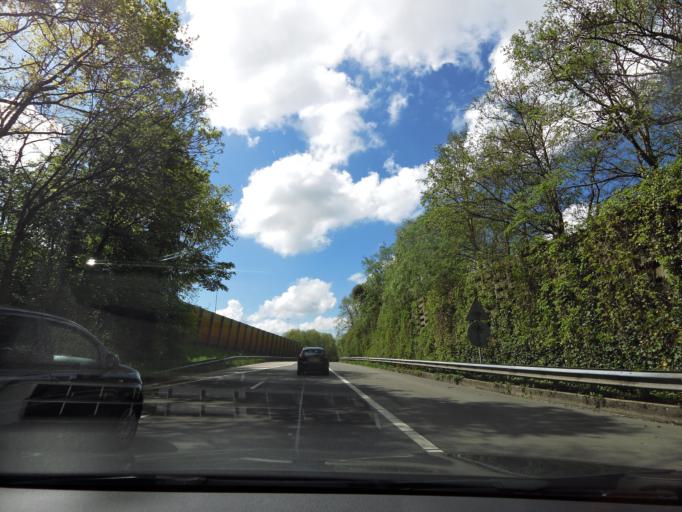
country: NL
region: North Holland
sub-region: Gemeente Amstelveen
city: Amstelveen
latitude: 52.3020
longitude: 4.8556
